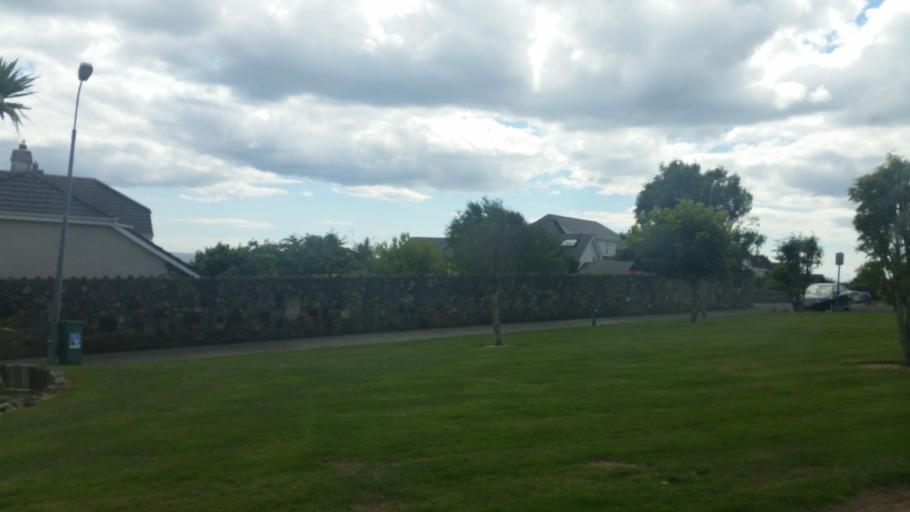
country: IE
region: Munster
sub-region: Waterford
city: Tra Mhor
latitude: 52.1541
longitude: -7.1681
